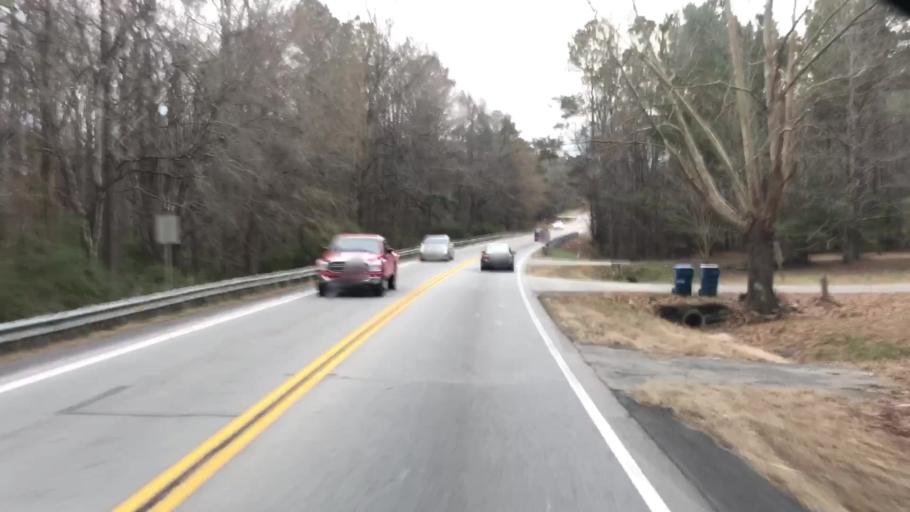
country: US
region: Georgia
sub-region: Barrow County
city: Auburn
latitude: 34.0364
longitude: -83.7743
